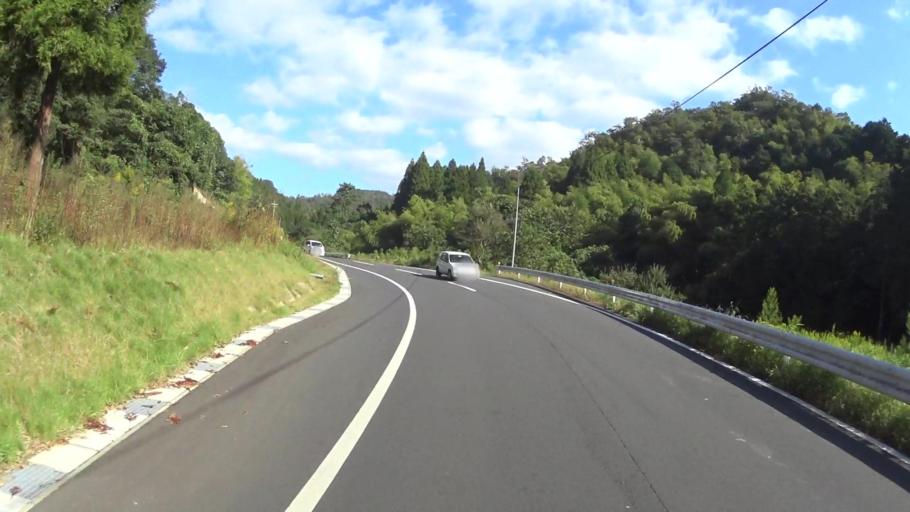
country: JP
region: Kyoto
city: Miyazu
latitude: 35.5841
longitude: 135.1613
